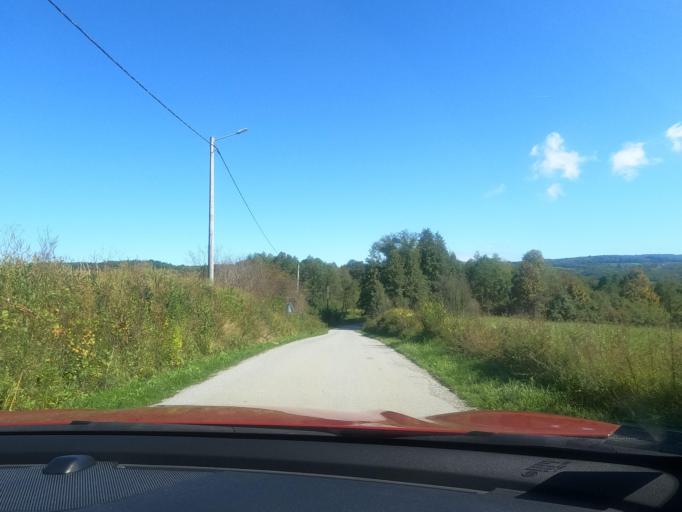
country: HR
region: Sisacko-Moslavacka
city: Petrinja
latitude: 45.3754
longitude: 16.2337
